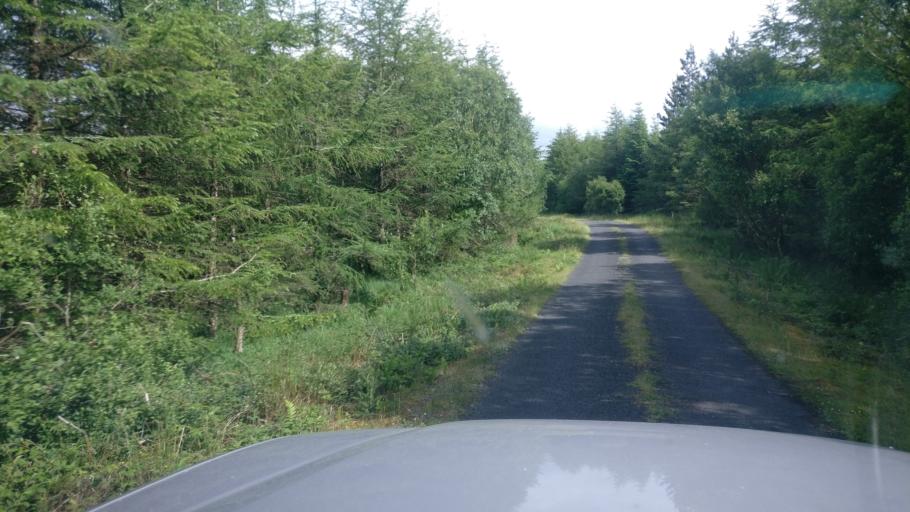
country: IE
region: Connaught
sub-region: County Galway
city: Gort
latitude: 53.0841
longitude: -8.6922
